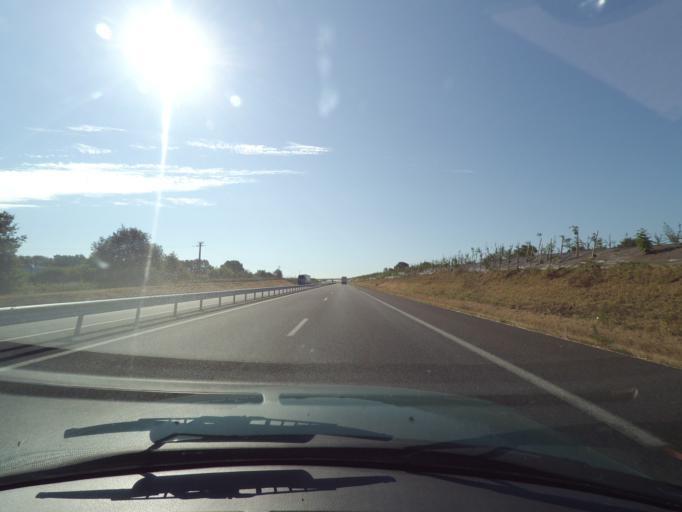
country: FR
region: Poitou-Charentes
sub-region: Departement de la Vienne
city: Savigny-Levescault
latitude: 46.4911
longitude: 0.4988
